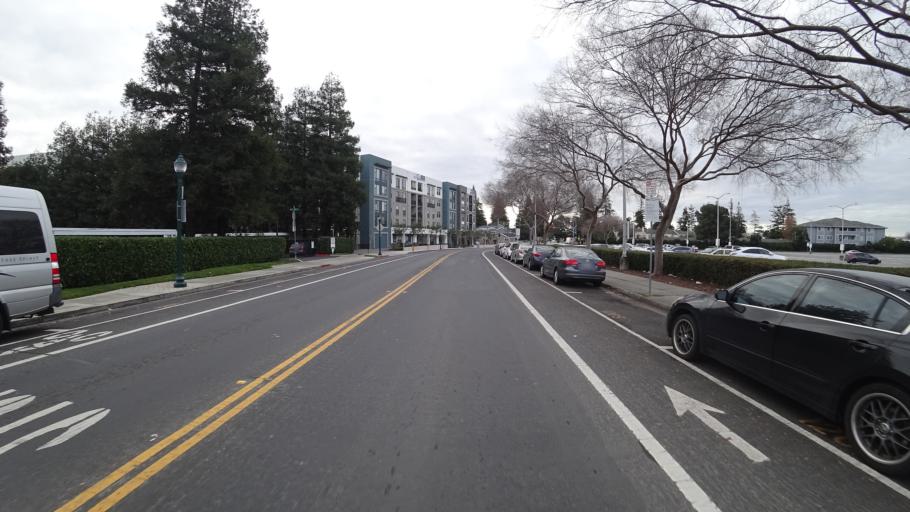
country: US
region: California
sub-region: Alameda County
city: Hayward
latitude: 37.6346
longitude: -122.0554
